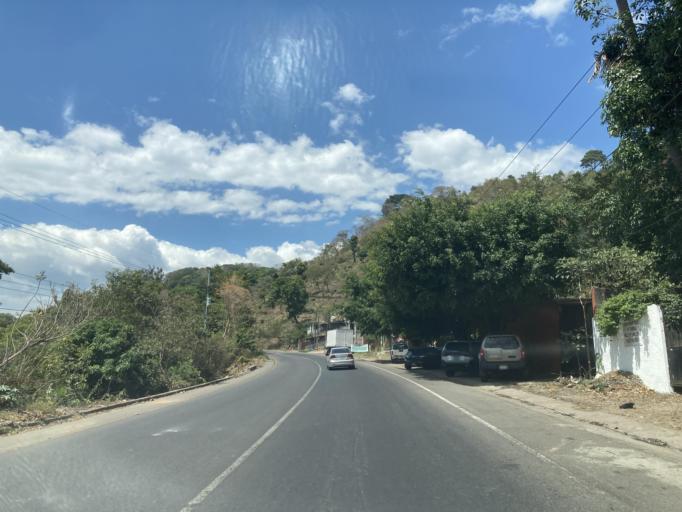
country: GT
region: Santa Rosa
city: Cuilapa
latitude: 14.2720
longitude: -90.3034
